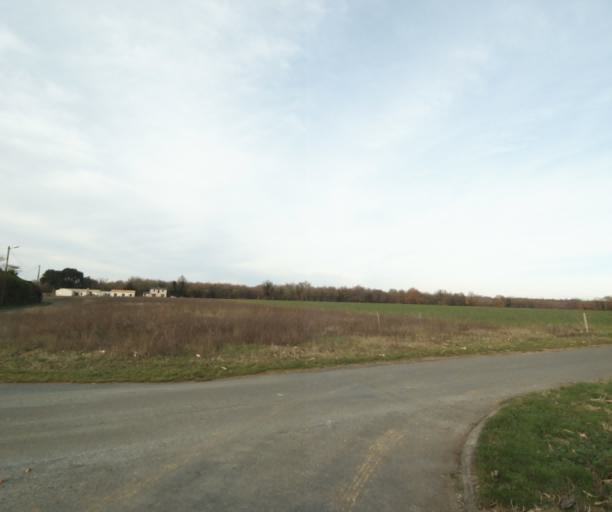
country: FR
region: Poitou-Charentes
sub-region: Departement de la Charente-Maritime
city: Saint-Hilaire-de-Villefranche
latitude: 45.8348
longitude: -0.5815
